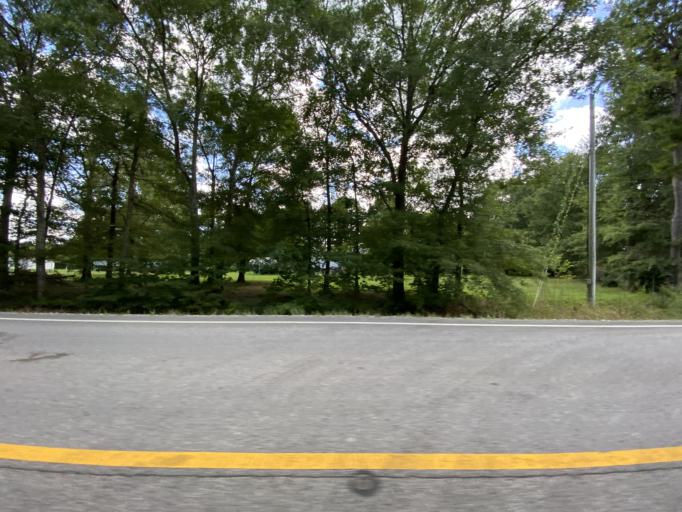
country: US
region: Alabama
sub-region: Lauderdale County
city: Underwood-Petersville
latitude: 34.9380
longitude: -87.8542
